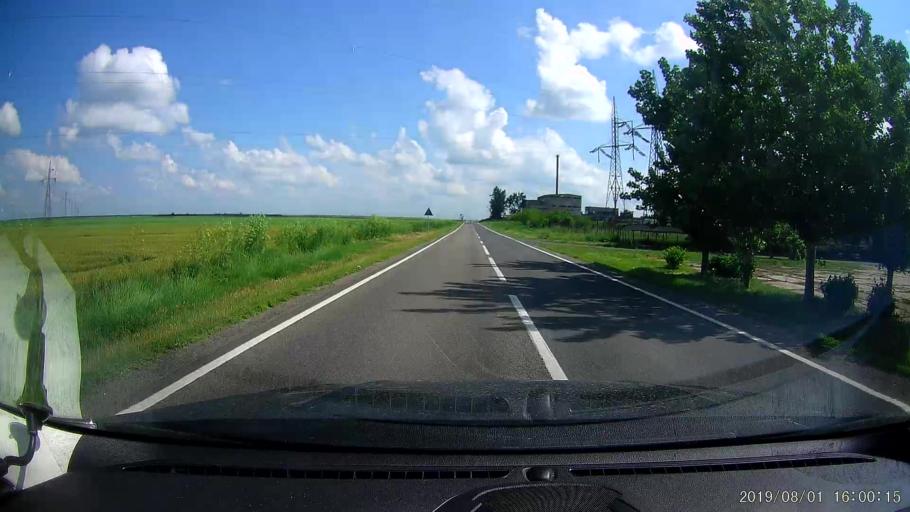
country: RO
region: Ialomita
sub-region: Comuna Ciulnita
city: Ciulnita
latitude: 44.5334
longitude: 27.3885
